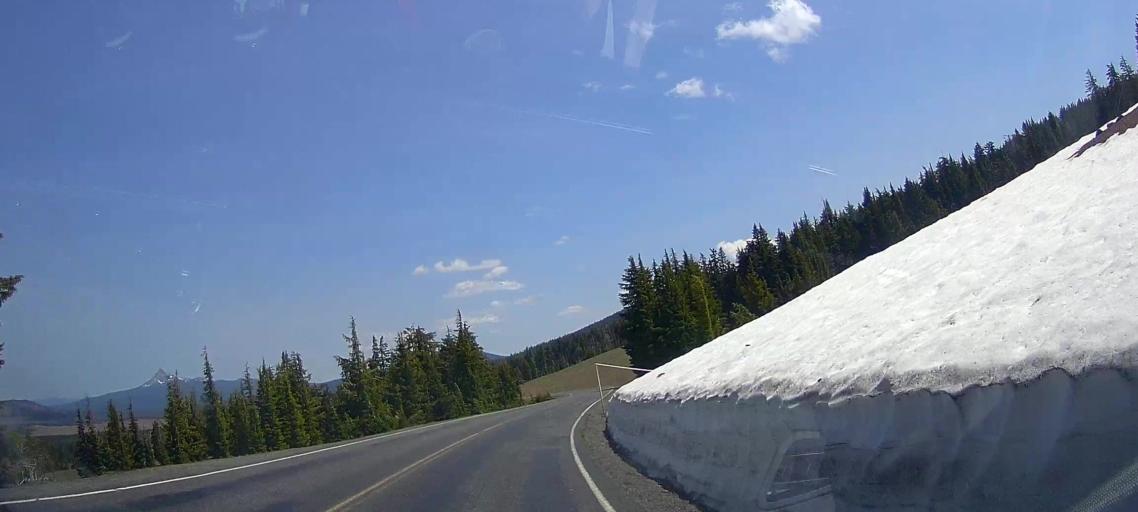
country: US
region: Oregon
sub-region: Jackson County
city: Shady Cove
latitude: 42.9830
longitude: -122.1516
